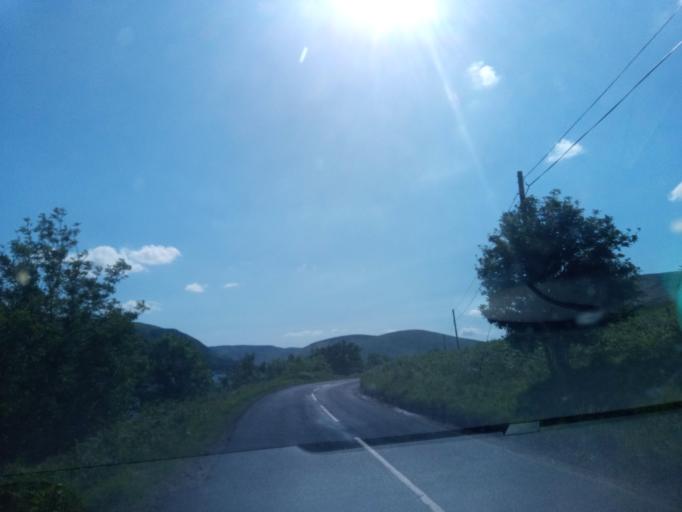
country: GB
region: Scotland
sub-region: The Scottish Borders
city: Peebles
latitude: 55.5030
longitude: -3.1677
